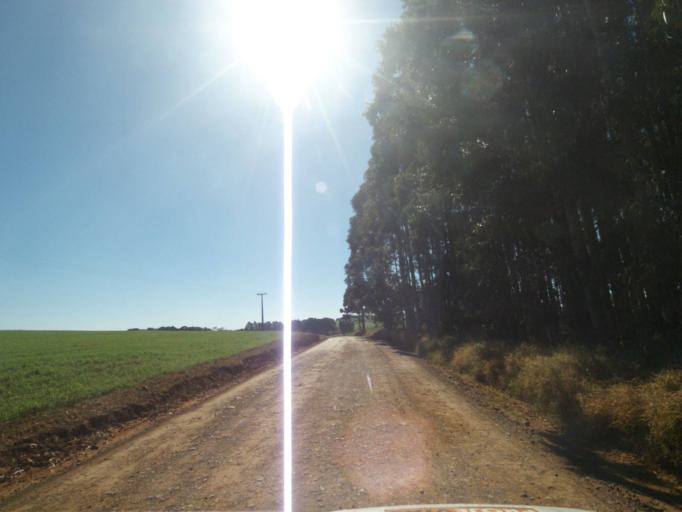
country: BR
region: Parana
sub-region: Tibagi
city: Tibagi
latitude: -24.6125
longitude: -50.6055
